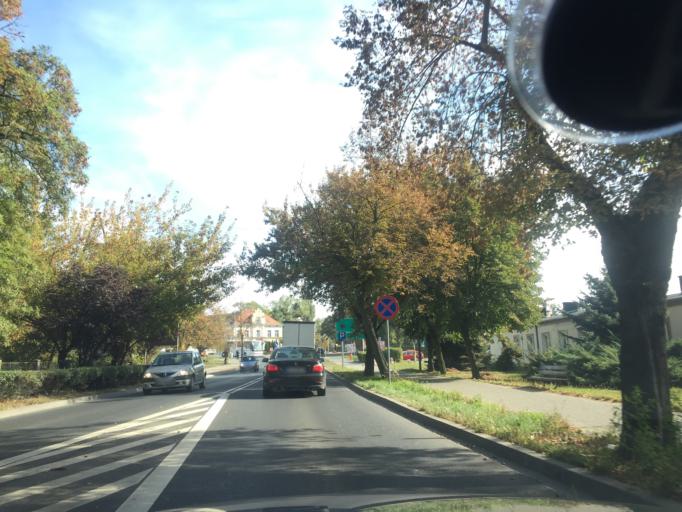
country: PL
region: Greater Poland Voivodeship
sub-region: Powiat wrzesinski
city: Wrzesnia
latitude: 52.3294
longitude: 17.5611
